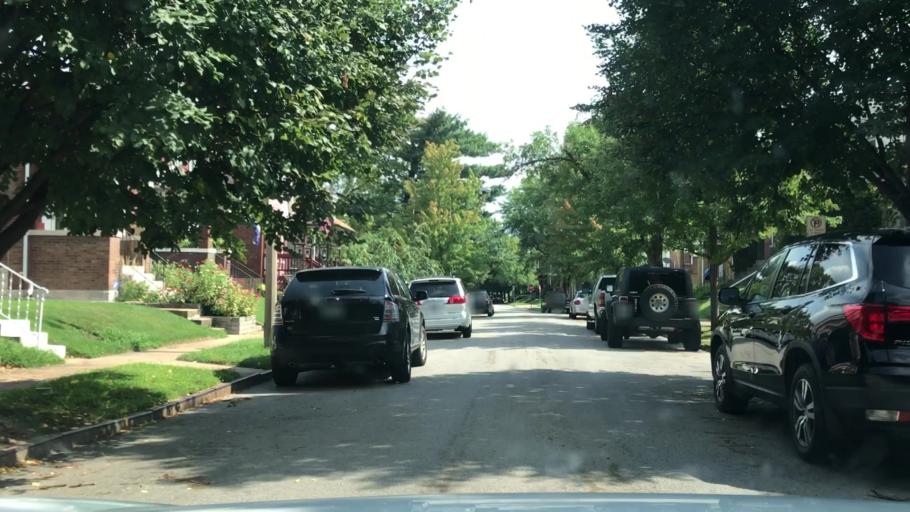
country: US
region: Missouri
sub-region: Saint Louis County
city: Lemay
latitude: 38.5790
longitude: -90.2786
